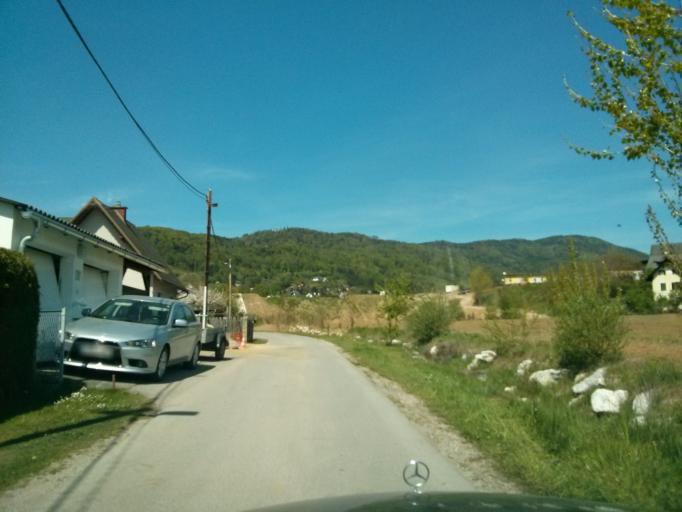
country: AT
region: Styria
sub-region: Politischer Bezirk Graz-Umgebung
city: Stattegg
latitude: 47.1351
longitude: 15.4198
